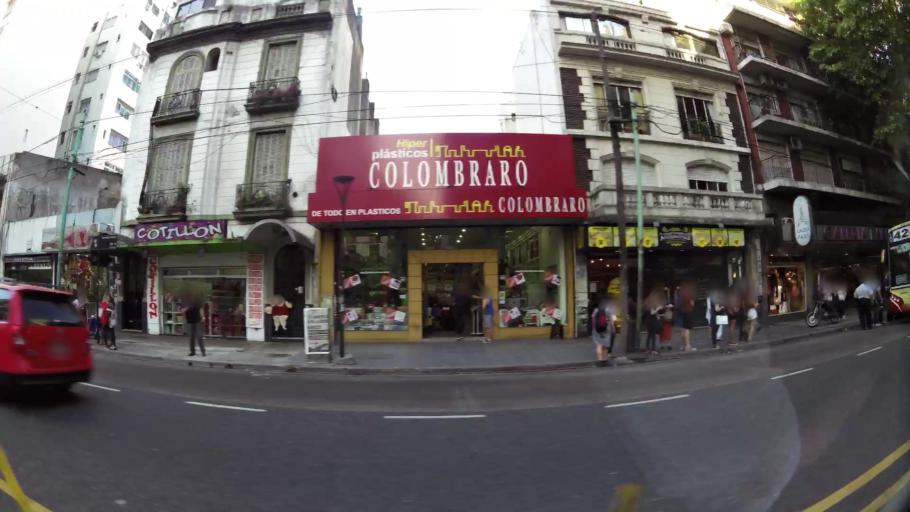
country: AR
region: Buenos Aires F.D.
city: Villa Santa Rita
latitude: -34.6172
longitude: -58.4370
